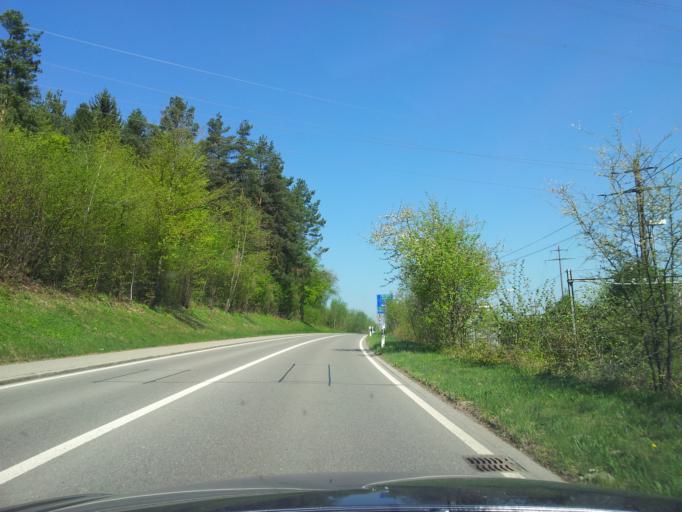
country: CH
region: Zurich
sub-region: Bezirk Dietikon
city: Birmensdorf
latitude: 47.3607
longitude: 8.4321
